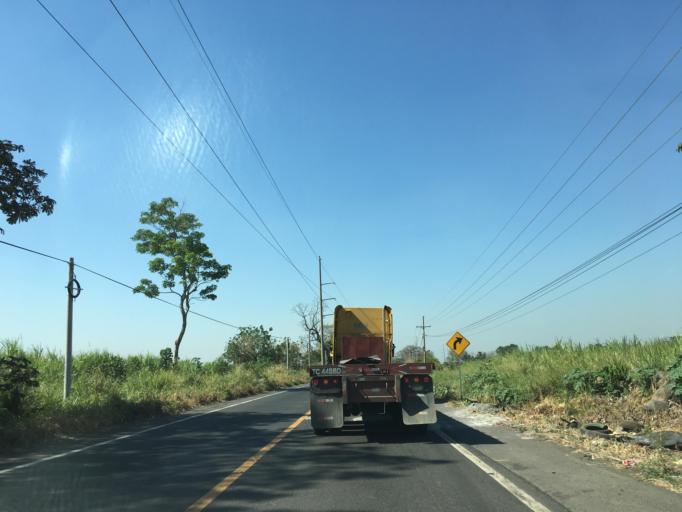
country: GT
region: Escuintla
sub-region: Municipio de Masagua
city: Masagua
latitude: 14.2479
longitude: -90.8079
